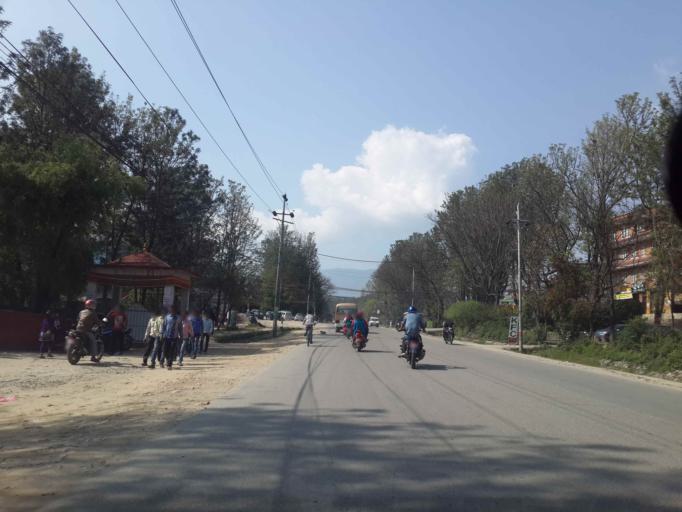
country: NP
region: Central Region
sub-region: Bagmati Zone
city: Kathmandu
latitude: 27.7338
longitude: 85.3430
